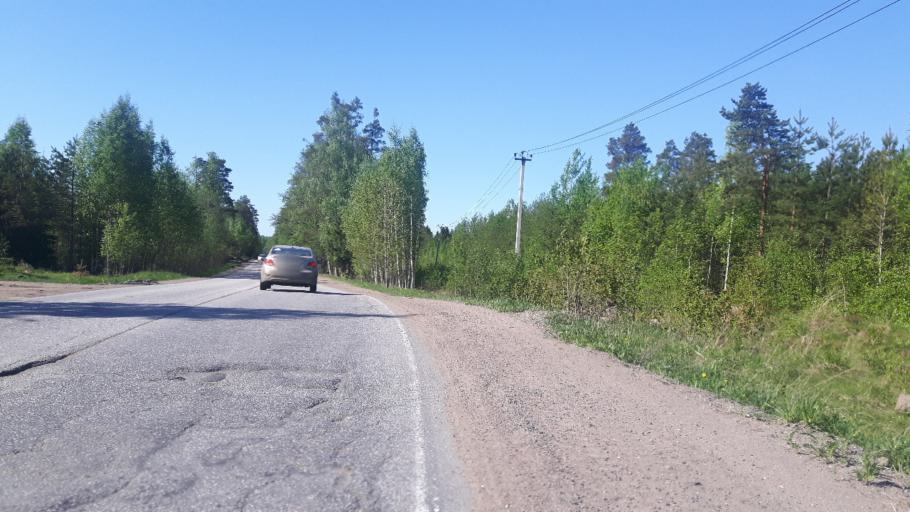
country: RU
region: Leningrad
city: Vyborg
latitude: 60.6469
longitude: 28.7477
